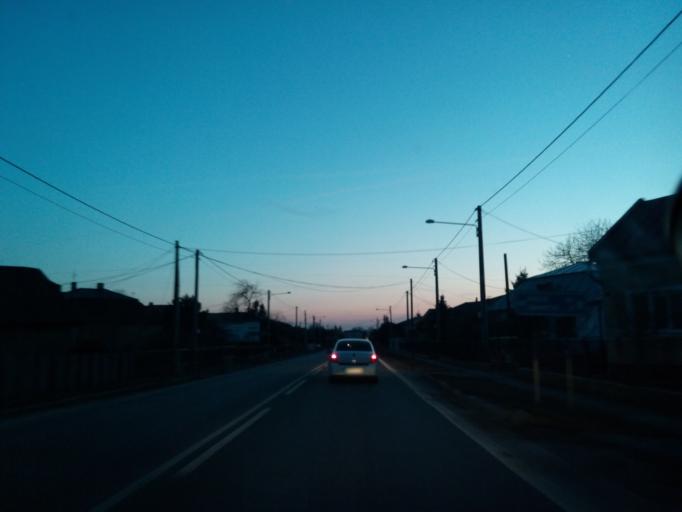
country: SK
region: Kosicky
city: Michalovce
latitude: 48.7329
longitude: 21.8836
